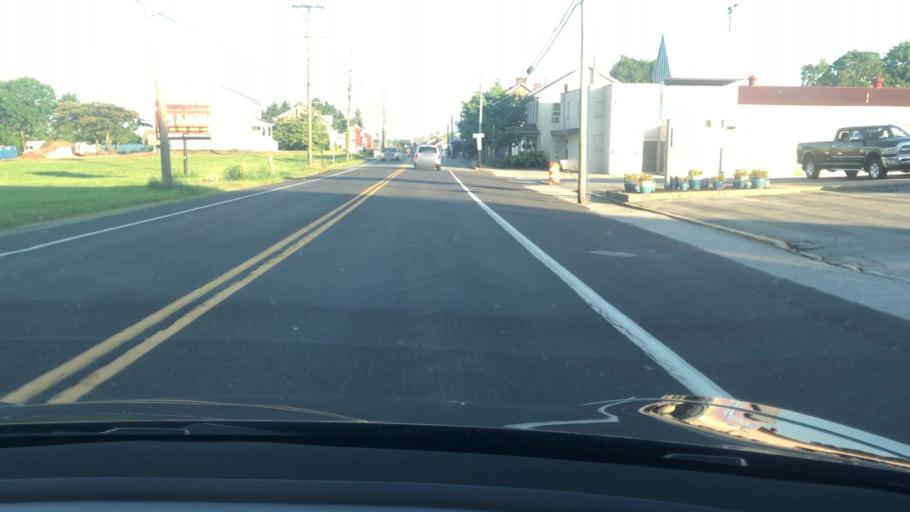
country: US
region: Pennsylvania
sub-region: York County
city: Dover
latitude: 40.0059
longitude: -76.8553
